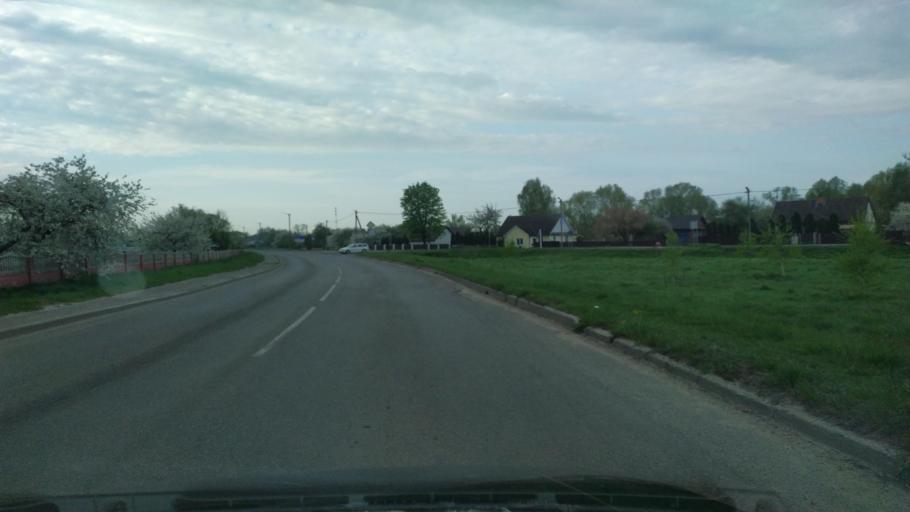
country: BY
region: Brest
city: Zhabinka
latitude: 52.2026
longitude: 24.0057
